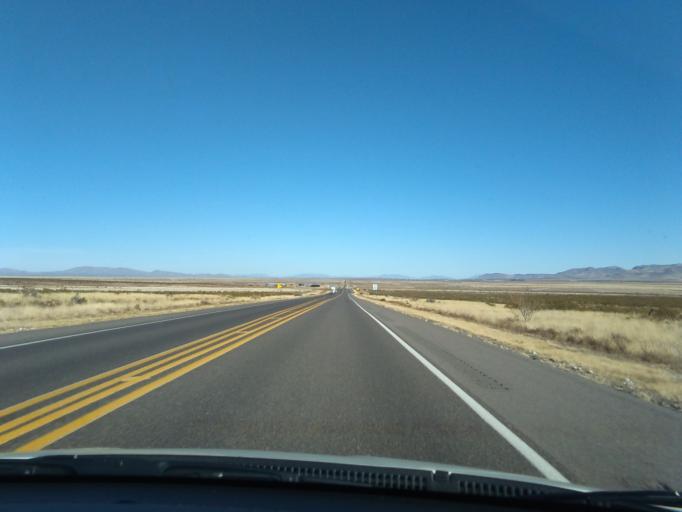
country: US
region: New Mexico
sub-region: Dona Ana County
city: Hatch
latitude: 32.5773
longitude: -107.3929
